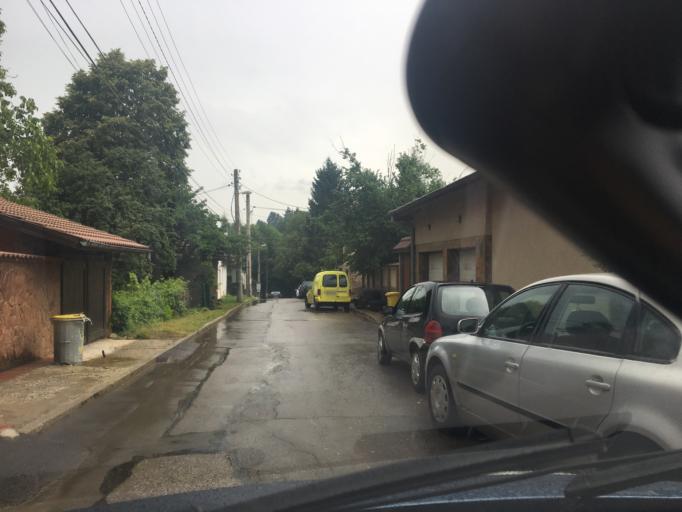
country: BG
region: Sofia-Capital
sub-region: Stolichna Obshtina
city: Sofia
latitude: 42.5852
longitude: 23.3526
